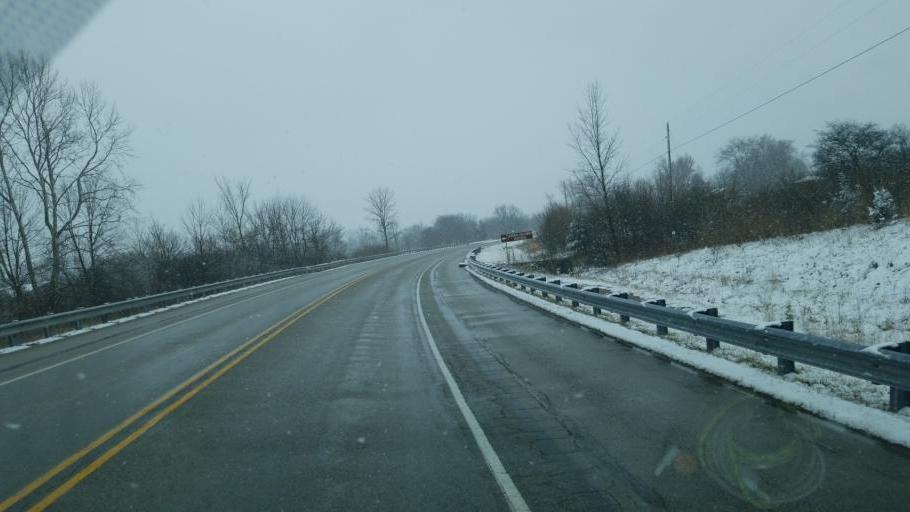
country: US
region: Indiana
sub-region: Wayne County
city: Richmond
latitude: 39.9159
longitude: -84.9523
